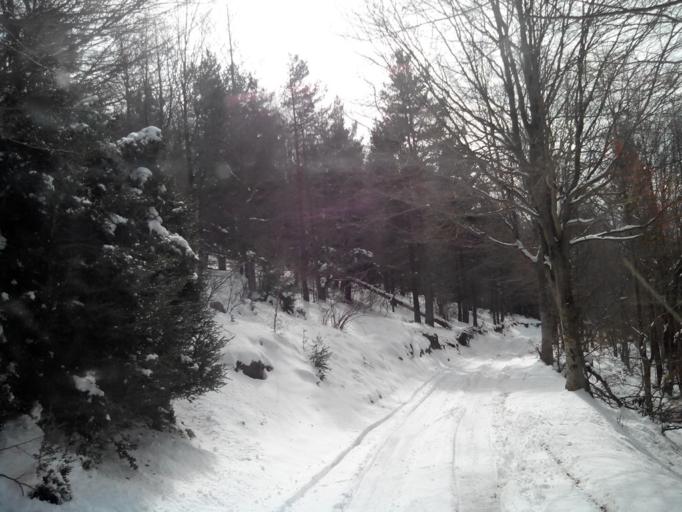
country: ES
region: Catalonia
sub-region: Provincia de Barcelona
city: Sant Julia de Cerdanyola
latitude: 42.1967
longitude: 1.9285
